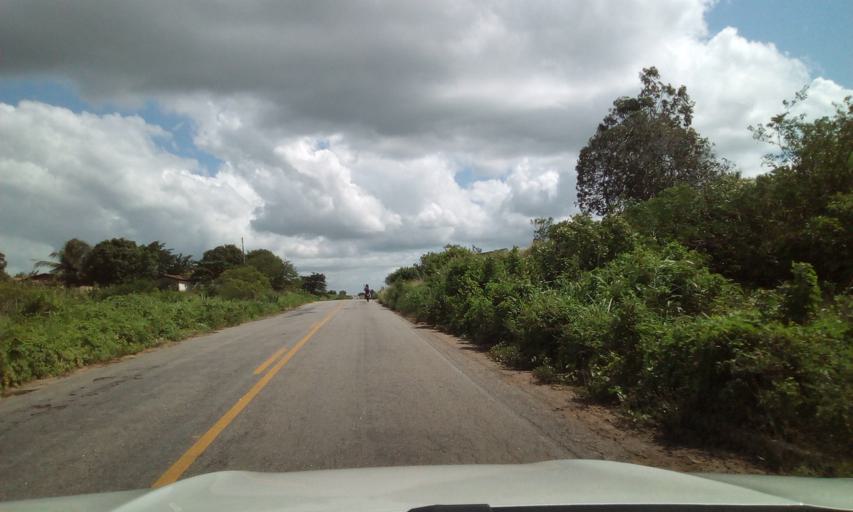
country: BR
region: Paraiba
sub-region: Guarabira
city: Guarabira
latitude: -6.8551
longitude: -35.4076
